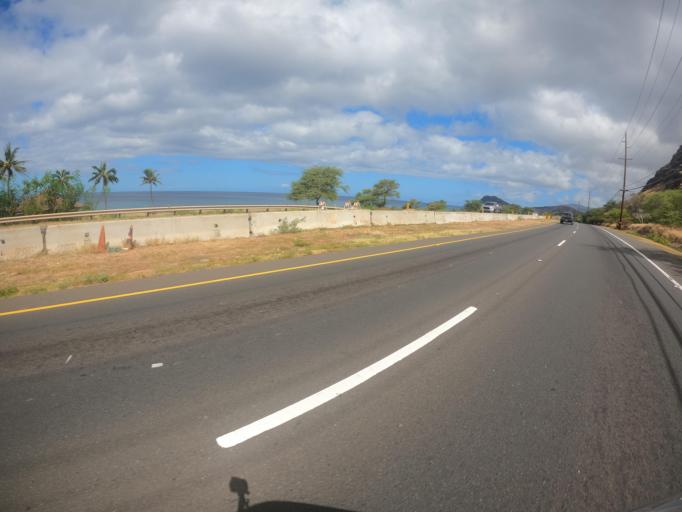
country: US
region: Hawaii
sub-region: Honolulu County
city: Nanakuli
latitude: 21.3617
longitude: -158.1313
